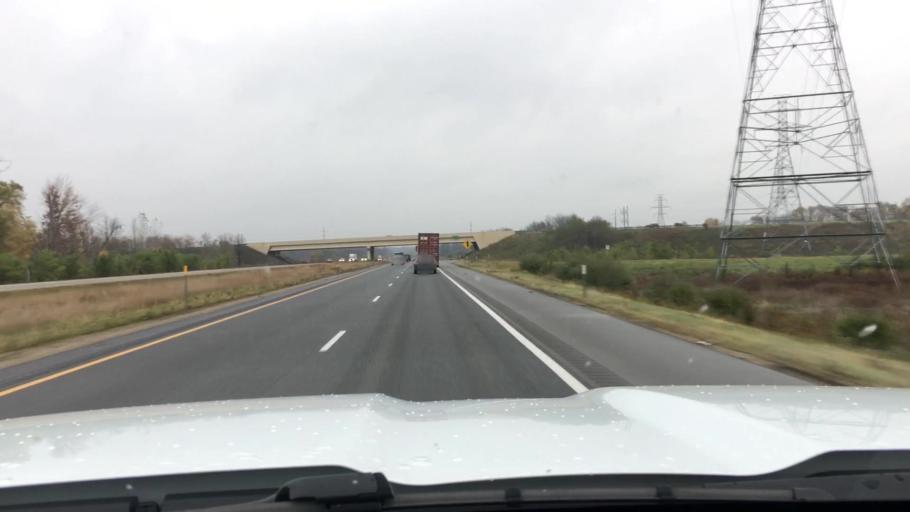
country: US
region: Michigan
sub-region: Kent County
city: Byron Center
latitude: 42.8472
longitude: -85.7661
